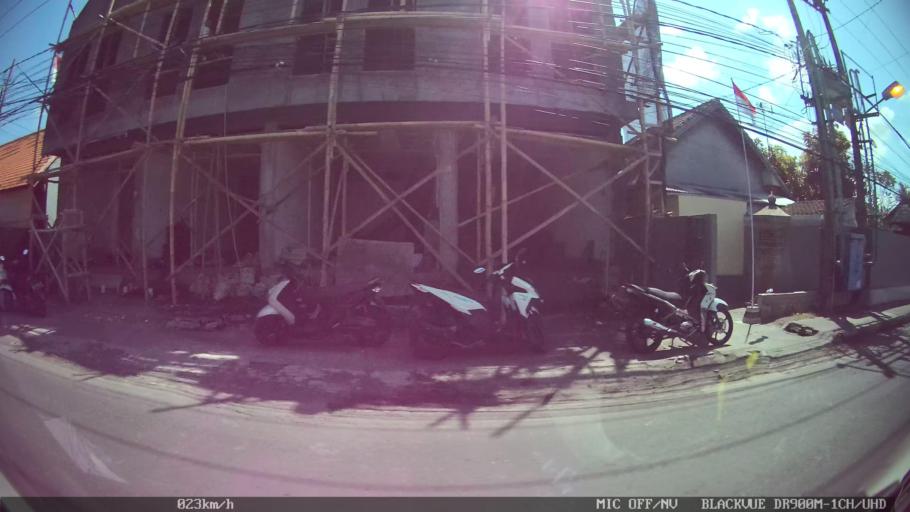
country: ID
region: Bali
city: Banjar Gunungpande
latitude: -8.6536
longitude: 115.1624
